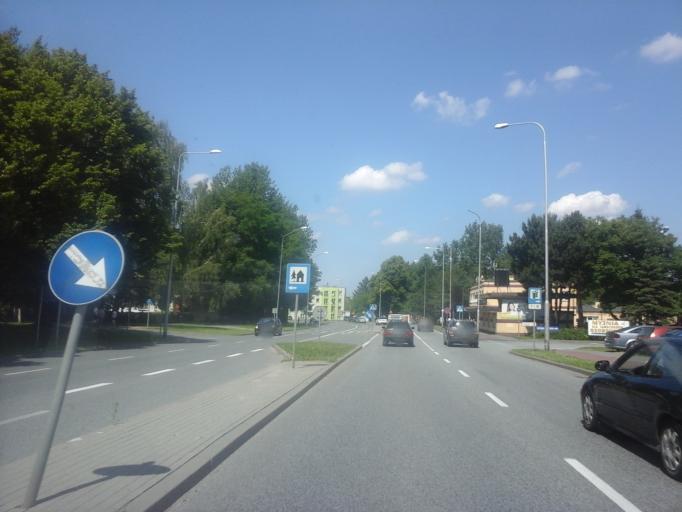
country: PL
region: West Pomeranian Voivodeship
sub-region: Koszalin
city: Koszalin
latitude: 54.1805
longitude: 16.1939
